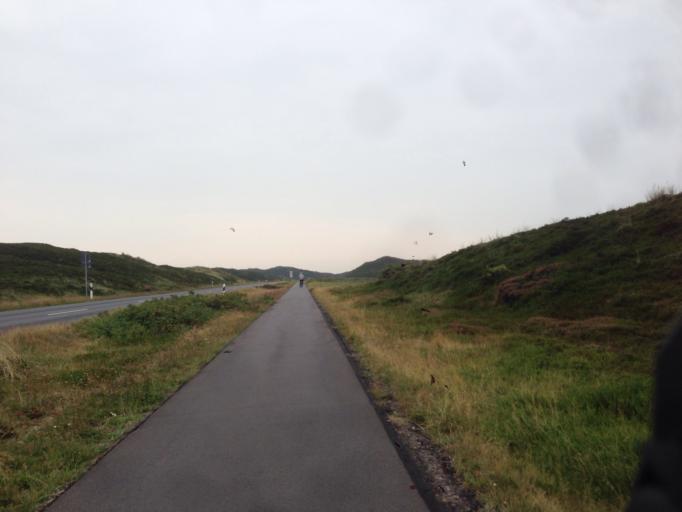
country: DE
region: Schleswig-Holstein
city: Norddorf
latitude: 54.7882
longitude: 8.2883
